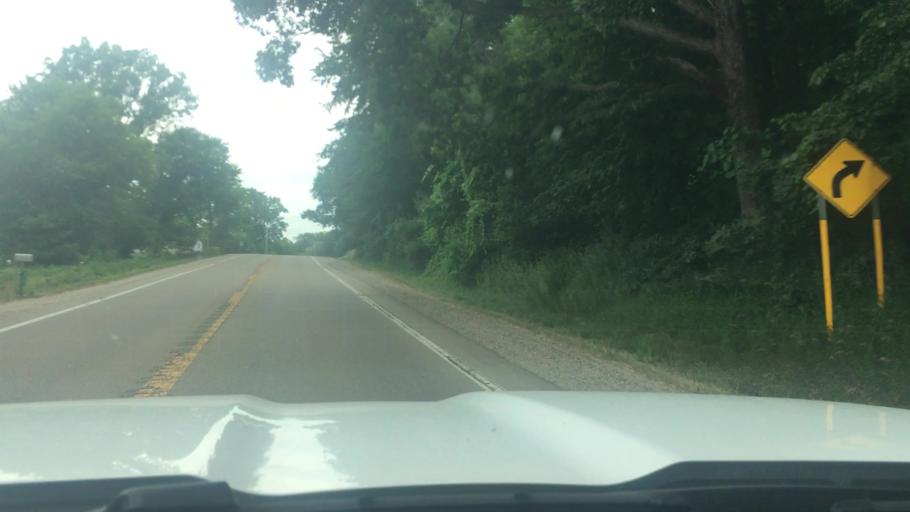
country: US
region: Michigan
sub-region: Ionia County
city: Saranac
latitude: 42.9345
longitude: -85.2678
